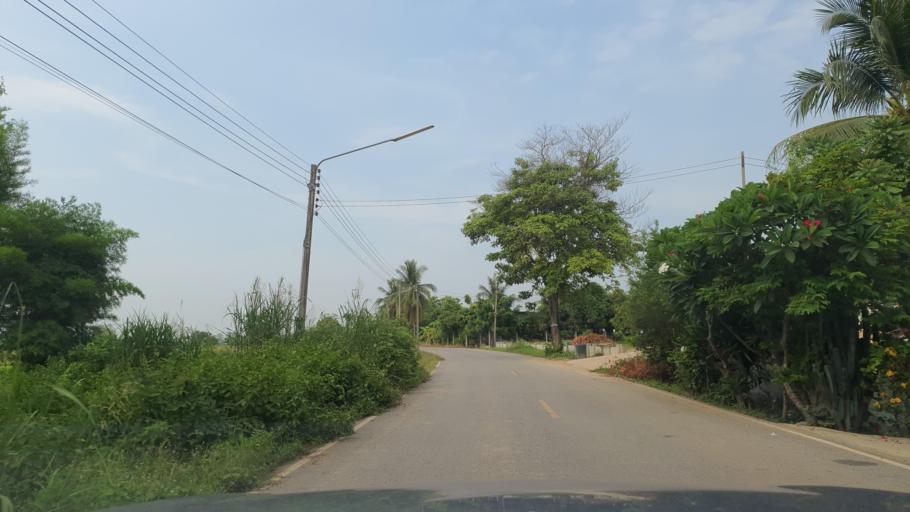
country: TH
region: Phitsanulok
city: Bang Rakam
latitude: 16.8087
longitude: 100.1623
